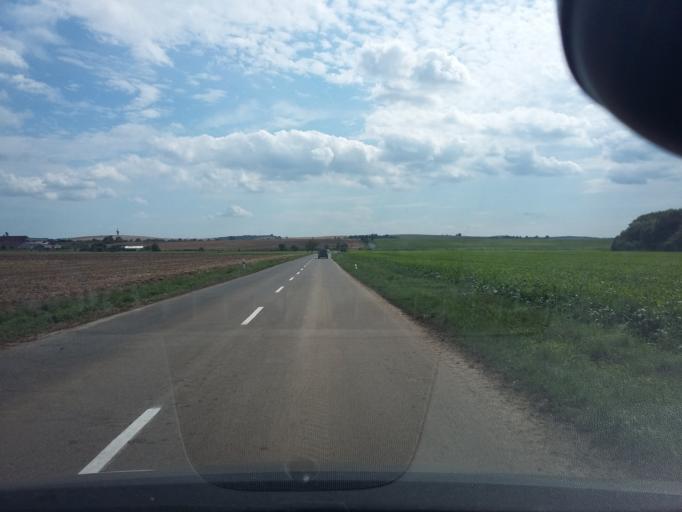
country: SK
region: Trnavsky
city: Gbely
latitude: 48.7392
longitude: 17.1684
